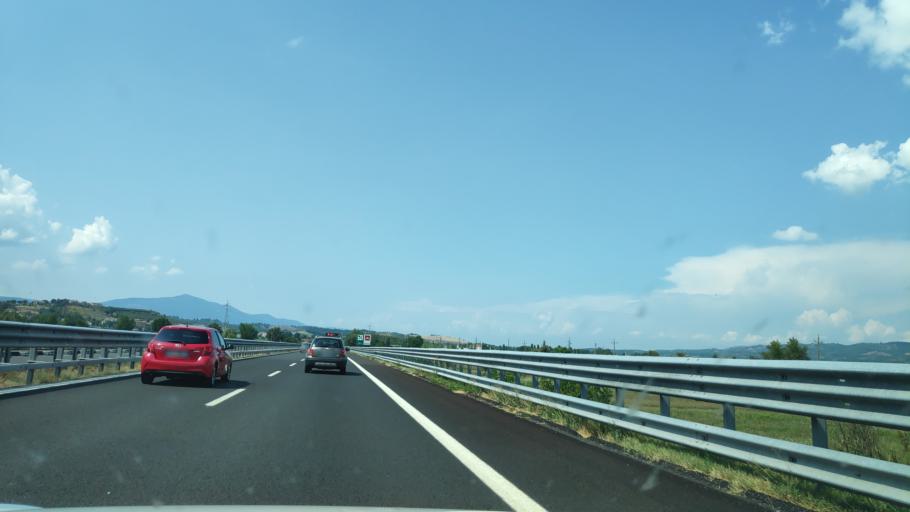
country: IT
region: Umbria
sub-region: Provincia di Terni
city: Fabro Scalo
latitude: 42.8642
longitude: 12.0331
